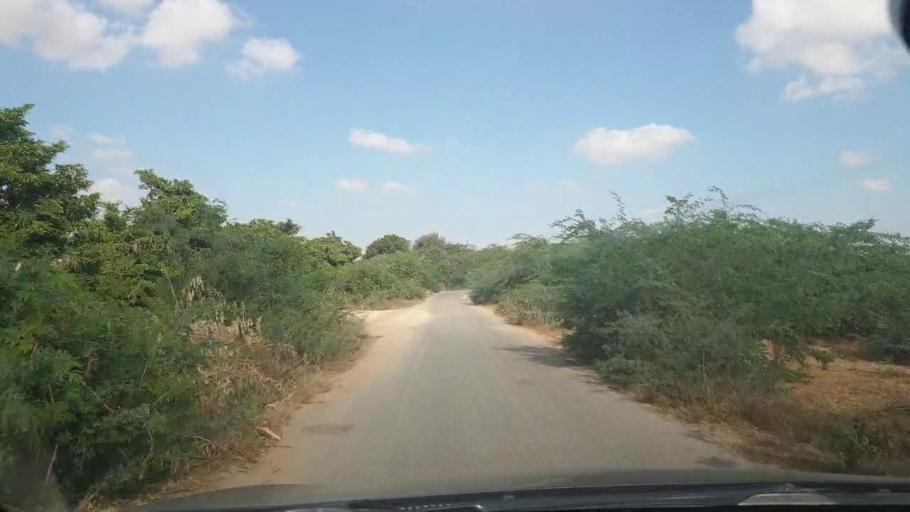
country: PK
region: Sindh
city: Malir Cantonment
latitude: 25.0577
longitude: 67.3911
